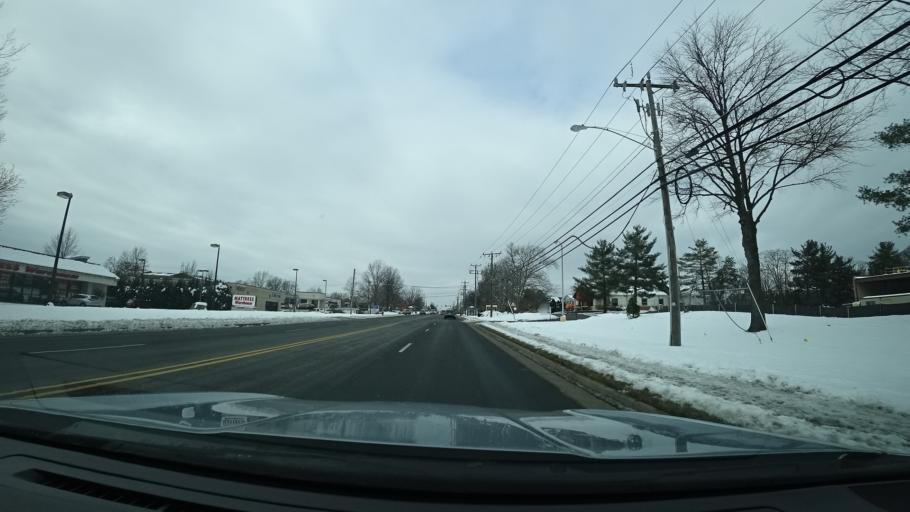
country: US
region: Virginia
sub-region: Fairfax County
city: Herndon
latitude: 38.9683
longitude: -77.3772
